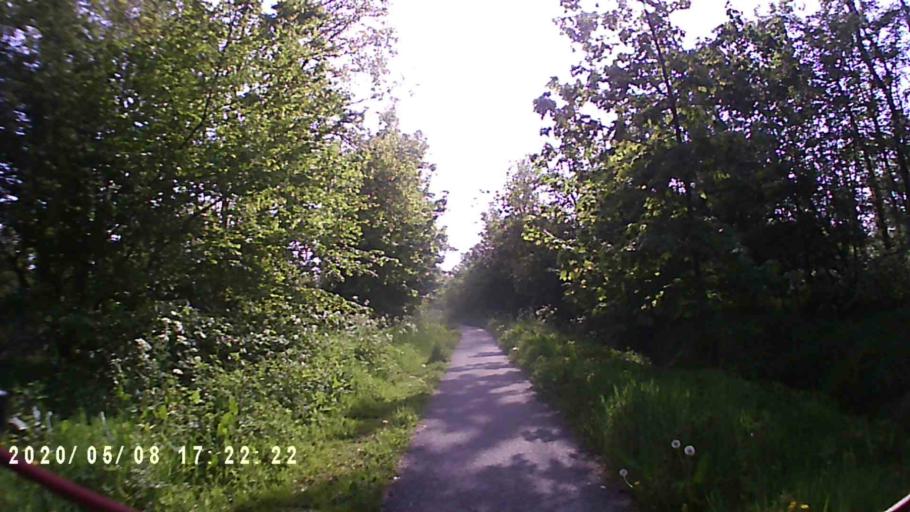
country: NL
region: Groningen
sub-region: Gemeente Winsum
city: Winsum
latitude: 53.3828
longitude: 6.5533
